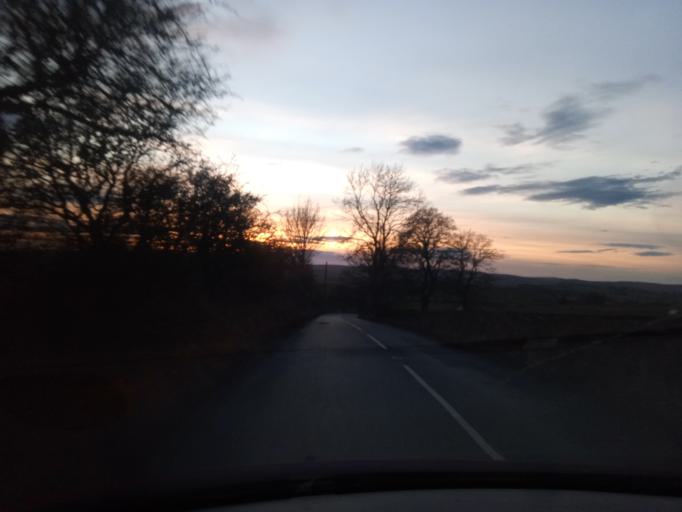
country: GB
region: England
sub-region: Northumberland
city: Otterburn
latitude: 55.2299
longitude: -2.1510
